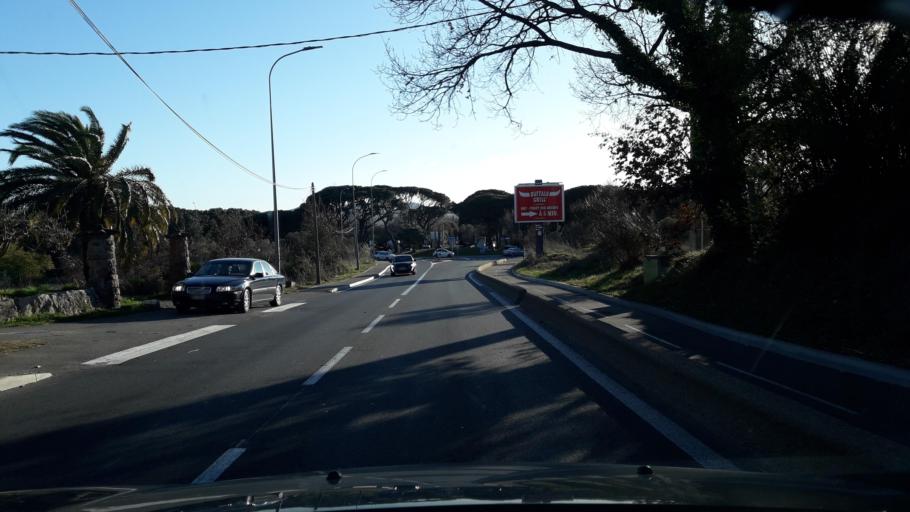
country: FR
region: Provence-Alpes-Cote d'Azur
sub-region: Departement du Var
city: Frejus
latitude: 43.4449
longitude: 6.7261
